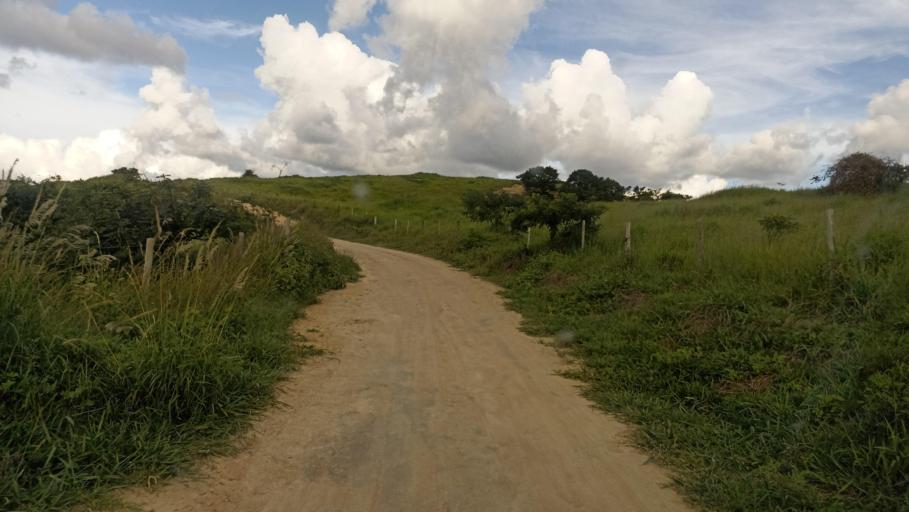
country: BR
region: Minas Gerais
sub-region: Almenara
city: Almenara
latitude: -16.5484
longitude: -40.4517
